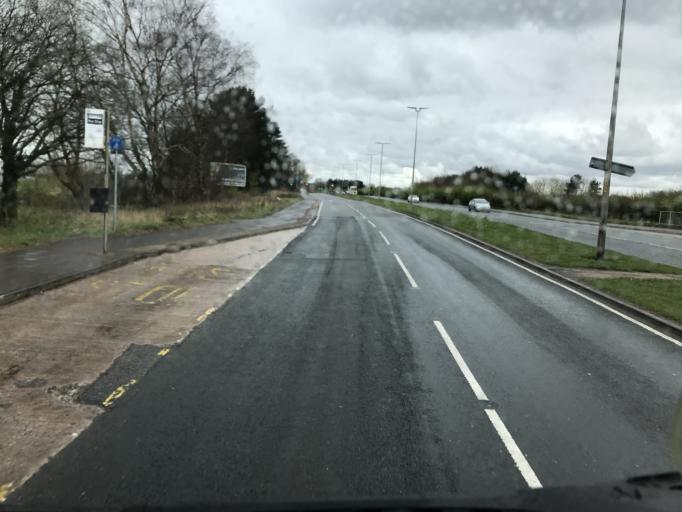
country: GB
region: England
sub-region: Trafford
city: Carrington
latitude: 53.4664
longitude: -2.3937
